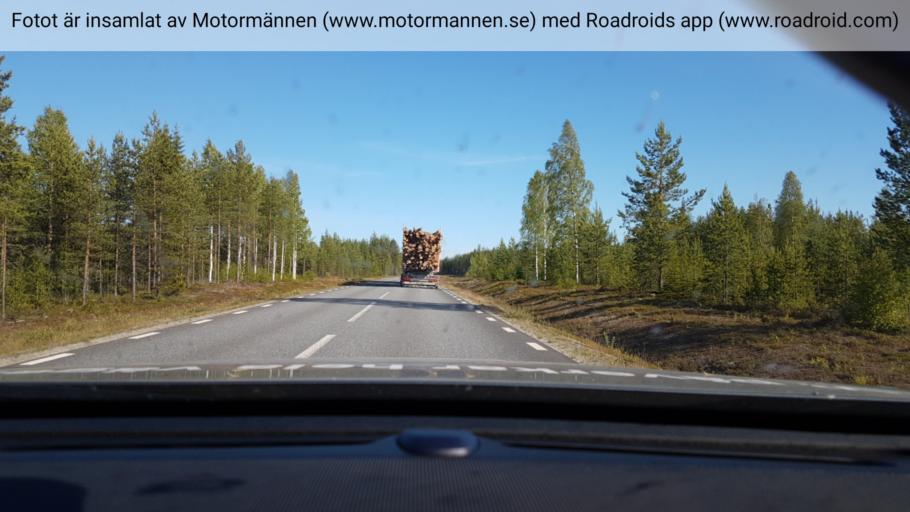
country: SE
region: Vaesterbotten
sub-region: Bjurholms Kommun
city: Bjurholm
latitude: 64.2950
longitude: 19.1813
